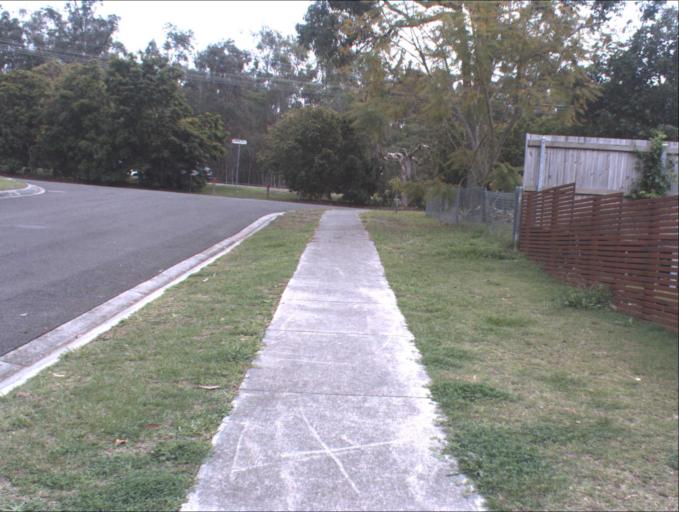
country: AU
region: Queensland
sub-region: Brisbane
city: Sunnybank Hills
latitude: -27.6589
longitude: 153.0255
